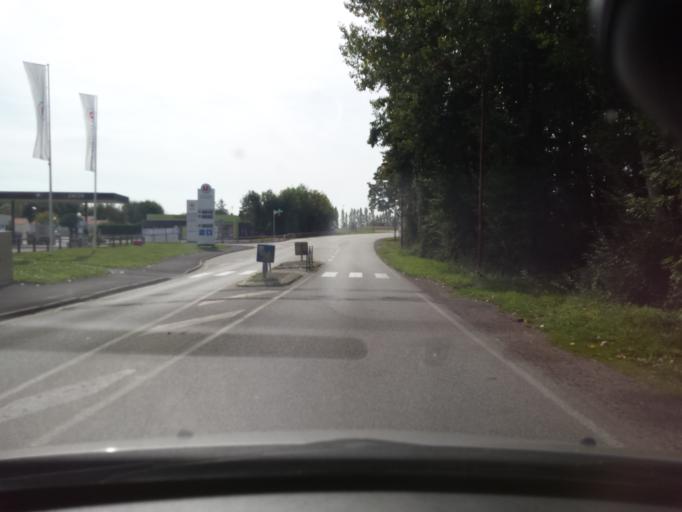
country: FR
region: Pays de la Loire
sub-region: Departement de la Vendee
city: Nieul-le-Dolent
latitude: 46.5720
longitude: -1.5100
